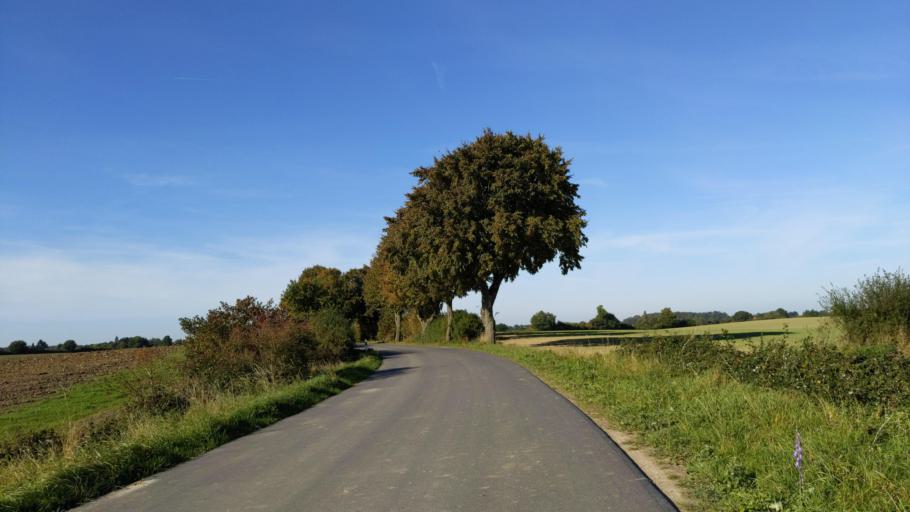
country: DE
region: Schleswig-Holstein
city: Ahrensbok
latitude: 54.0275
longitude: 10.6159
